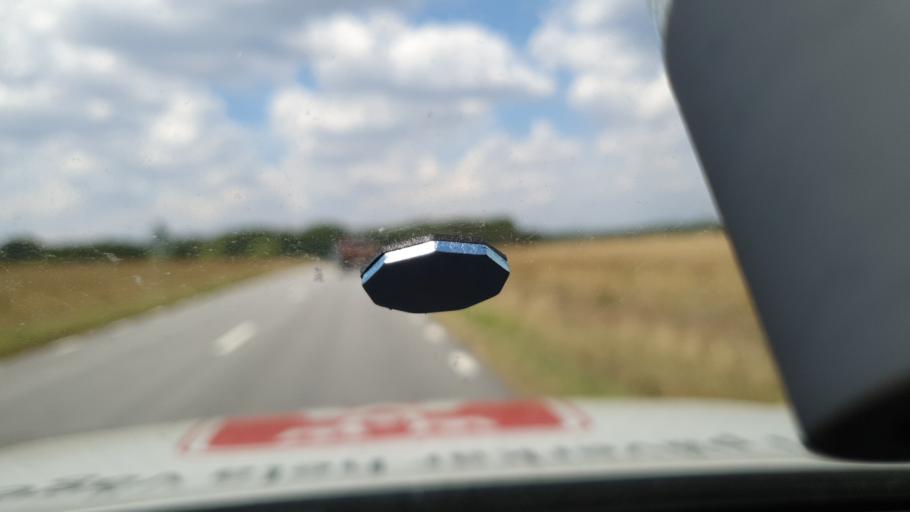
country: SE
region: Skane
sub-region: Sjobo Kommun
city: Blentarp
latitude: 55.5824
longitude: 13.6082
